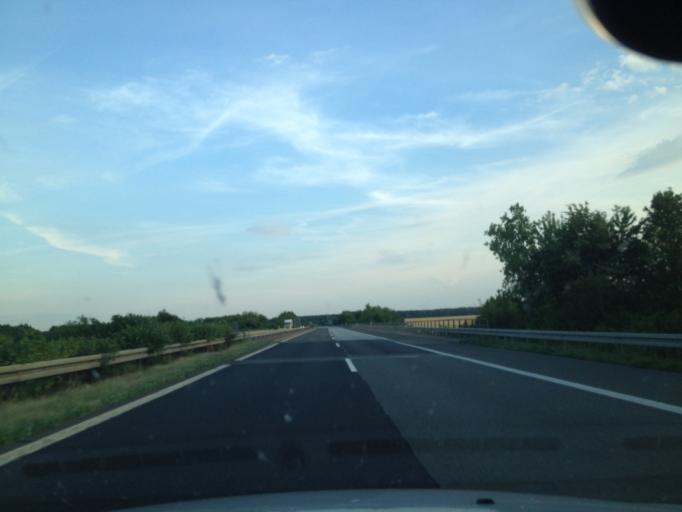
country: DE
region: Bavaria
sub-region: Regierungsbezirk Unterfranken
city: Biebelried
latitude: 49.7365
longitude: 10.1053
